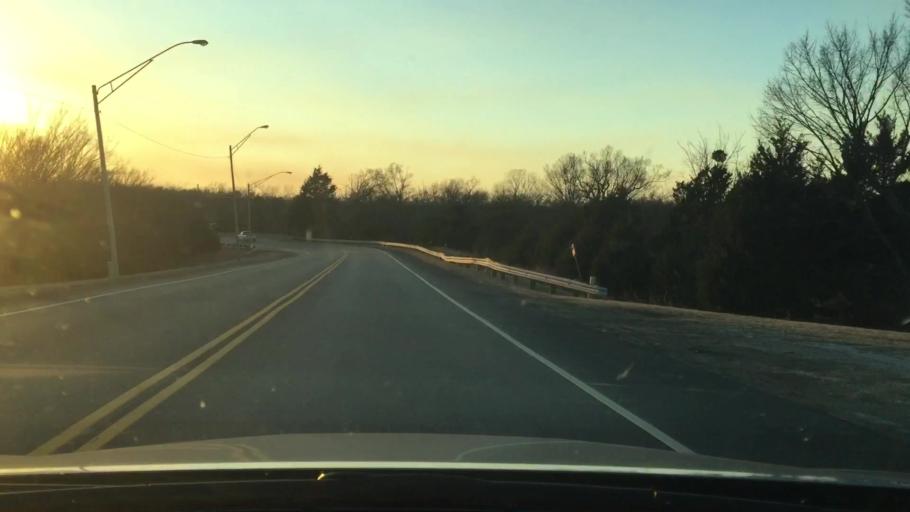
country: US
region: Oklahoma
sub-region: Carter County
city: Ardmore
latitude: 34.1750
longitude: -97.1738
